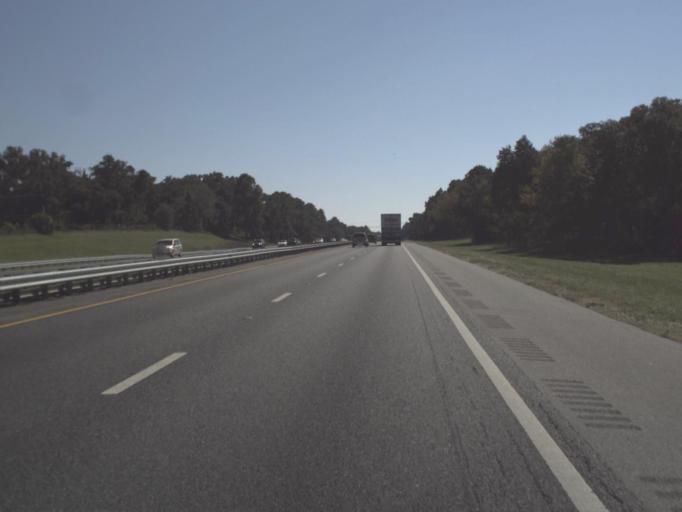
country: US
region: Florida
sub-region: Sumter County
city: Wildwood
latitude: 28.8215
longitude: -82.0224
